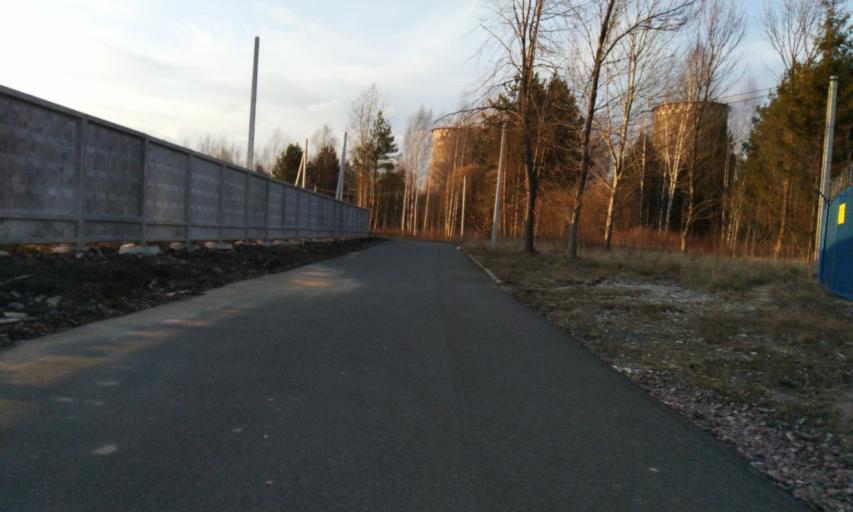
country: RU
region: Leningrad
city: Novoye Devyatkino
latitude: 60.0750
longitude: 30.4689
